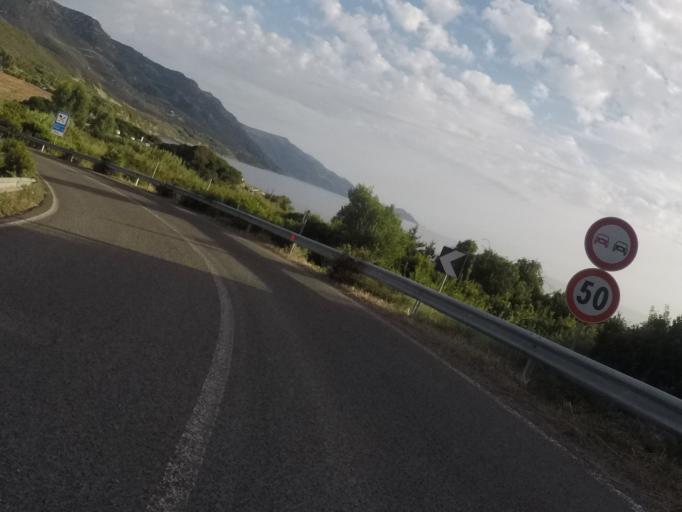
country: IT
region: Sardinia
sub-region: Provincia di Sassari
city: Alghero
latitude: 40.4980
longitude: 8.3679
